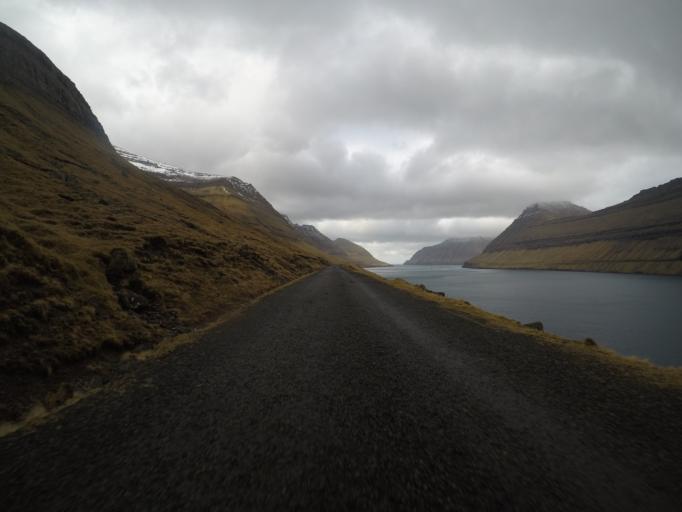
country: FO
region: Nordoyar
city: Klaksvik
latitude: 62.3123
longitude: -6.5498
